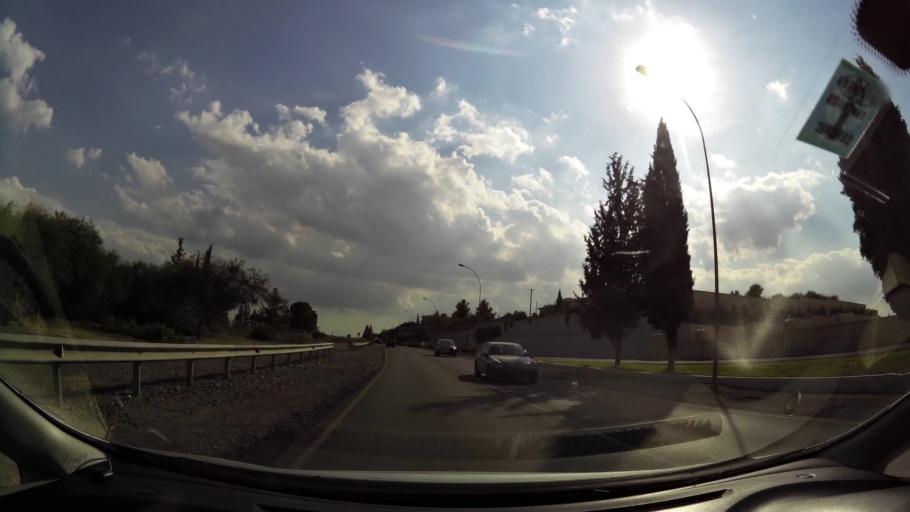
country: CY
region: Lefkosia
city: Nicosia
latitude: 35.1538
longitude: 33.3086
